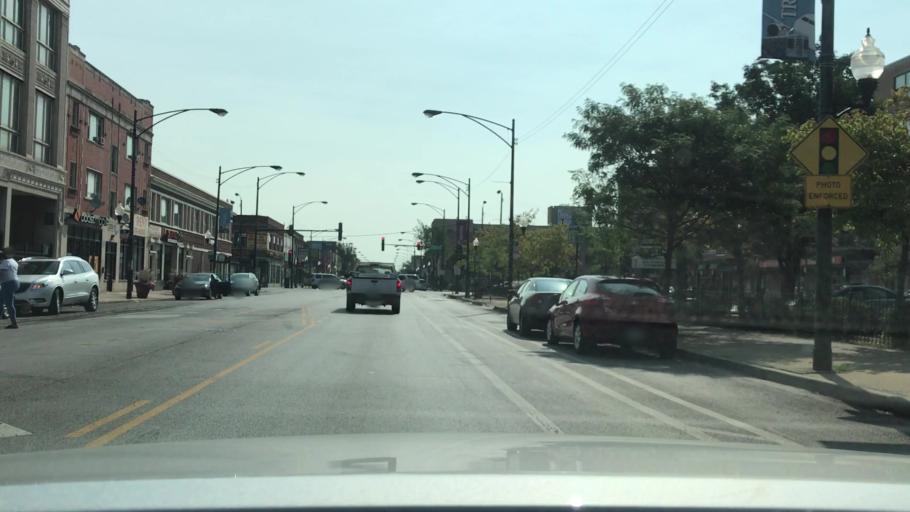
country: US
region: Illinois
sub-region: Cook County
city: Hometown
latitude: 41.7789
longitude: -87.7043
